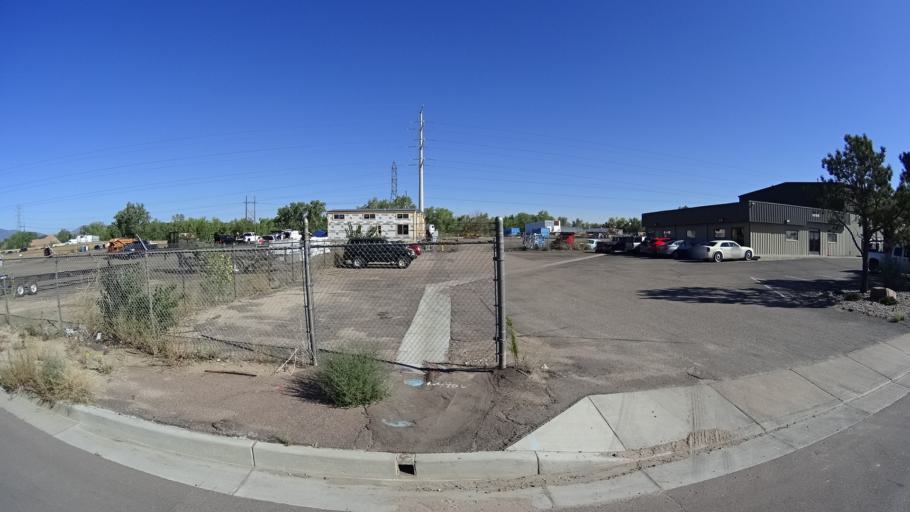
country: US
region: Colorado
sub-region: El Paso County
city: Stratmoor
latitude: 38.7878
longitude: -104.7681
